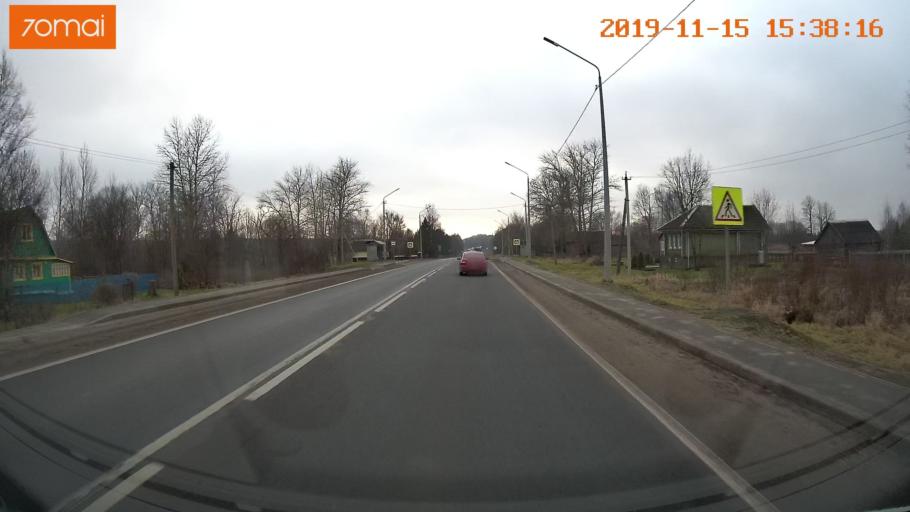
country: RU
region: Jaroslavl
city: Danilov
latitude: 58.0313
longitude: 40.0822
